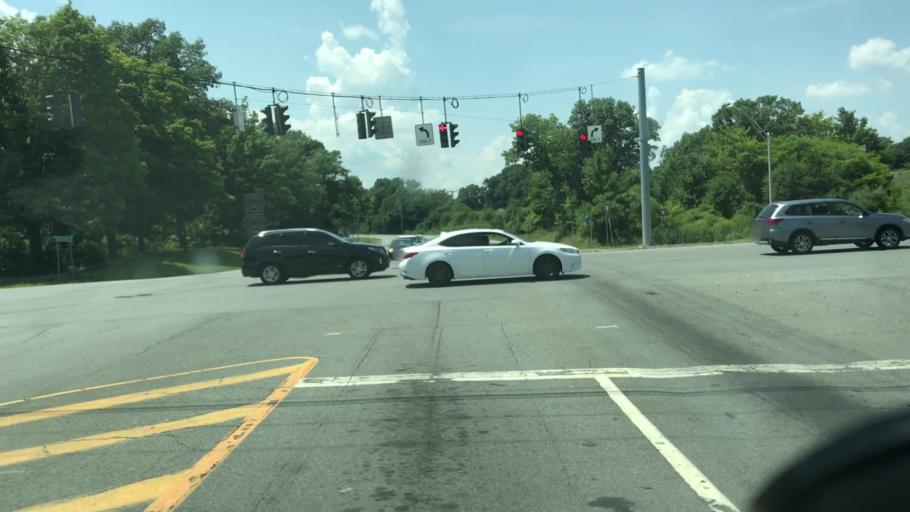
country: US
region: New York
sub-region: Orange County
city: Maybrook
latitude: 41.5101
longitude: -74.2067
